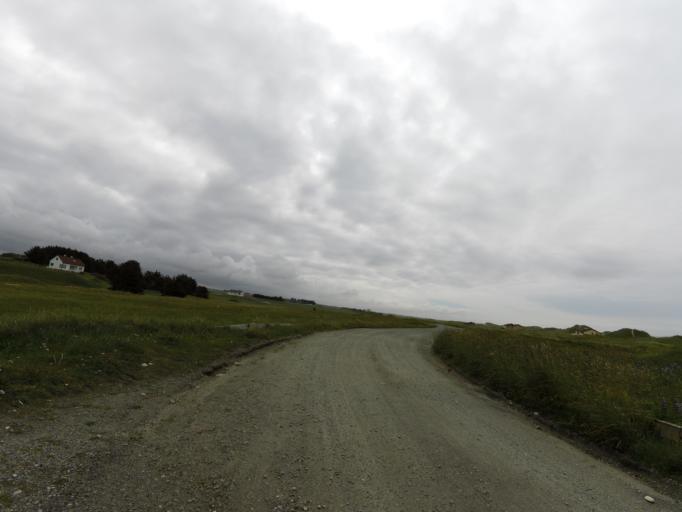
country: NO
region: Rogaland
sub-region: Klepp
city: Kleppe
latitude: 58.8094
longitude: 5.5509
